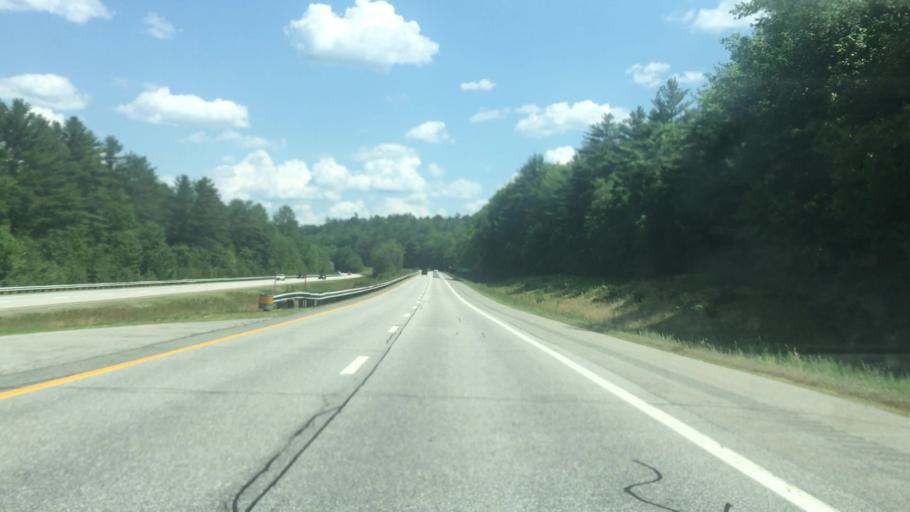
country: US
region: New Hampshire
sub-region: Merrimack County
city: Henniker
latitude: 43.2810
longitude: -71.8304
